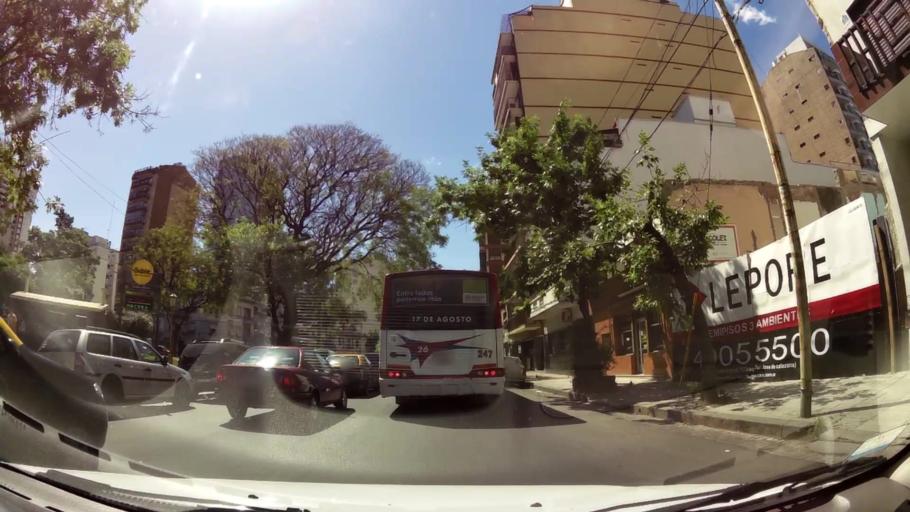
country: AR
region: Buenos Aires F.D.
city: Villa Santa Rita
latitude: -34.6314
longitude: -58.4418
